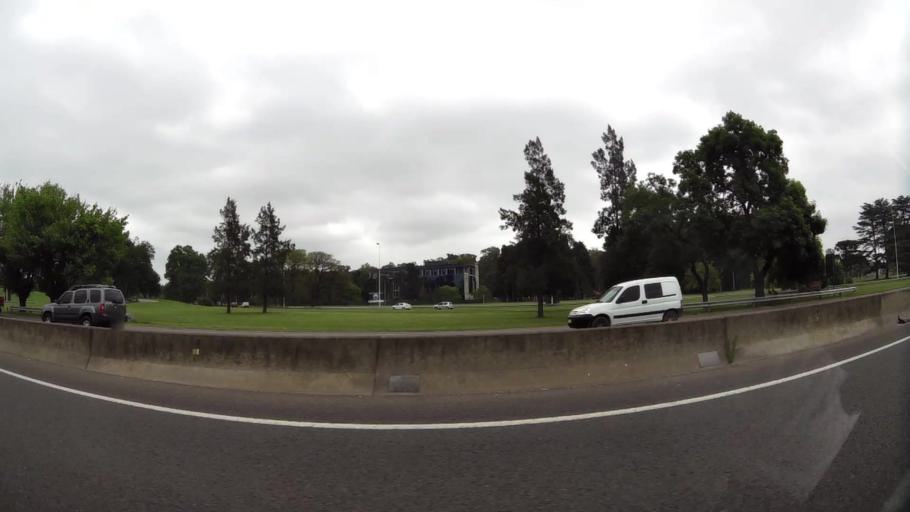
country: AR
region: Buenos Aires
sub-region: Partido de Ezeiza
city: Ezeiza
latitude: -34.7820
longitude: -58.5247
